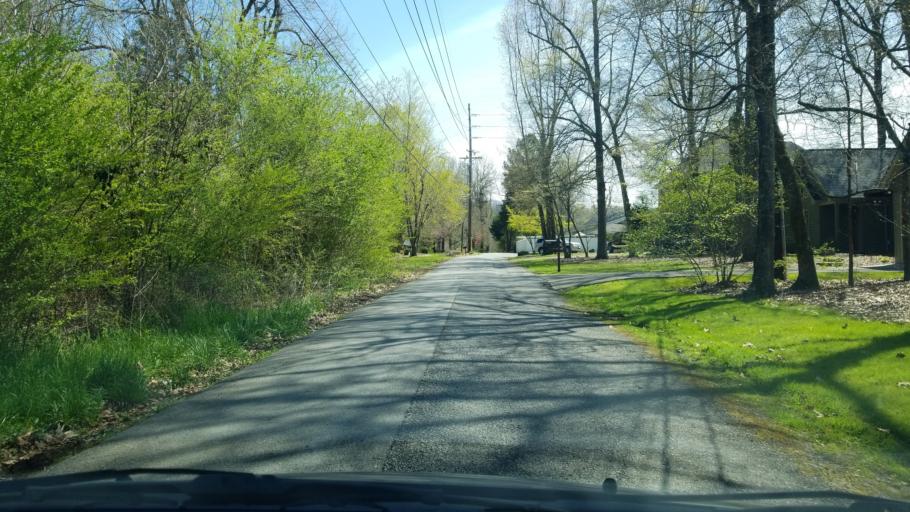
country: US
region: Tennessee
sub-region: Hamilton County
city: Middle Valley
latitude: 35.1639
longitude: -85.2085
